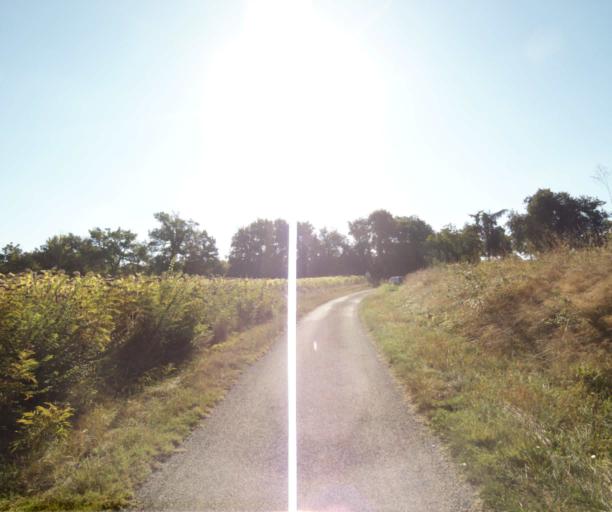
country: FR
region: Midi-Pyrenees
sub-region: Departement du Tarn-et-Garonne
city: Verdun-sur-Garonne
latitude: 43.8638
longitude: 1.2228
